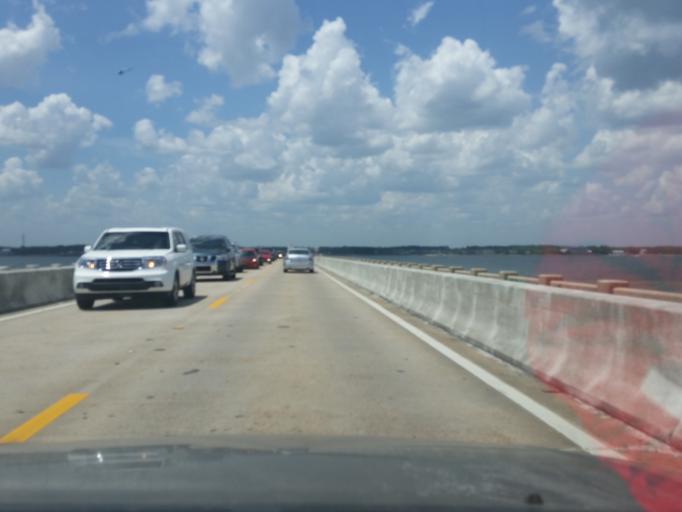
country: US
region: Florida
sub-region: Santa Rosa County
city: Navarre
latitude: 30.3866
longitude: -86.8624
